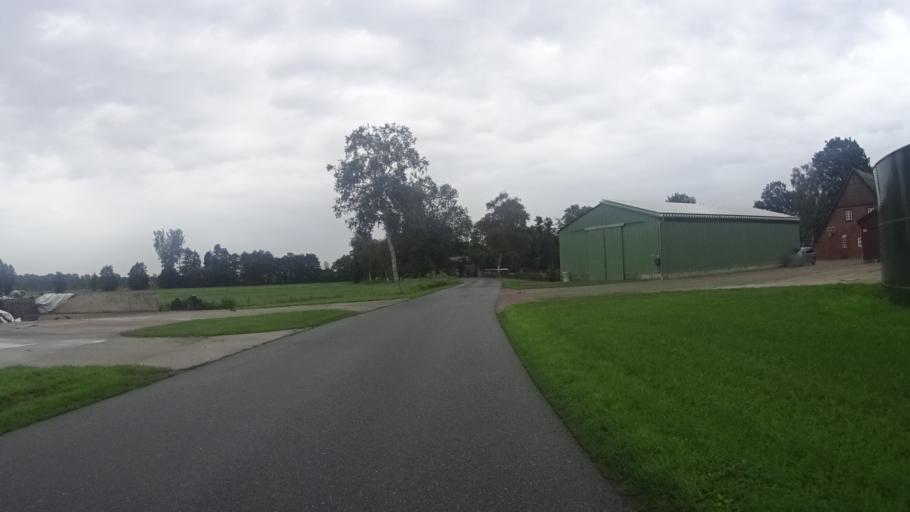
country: DE
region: Schleswig-Holstein
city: Kiebitzreihe
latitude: 53.7880
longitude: 9.5982
